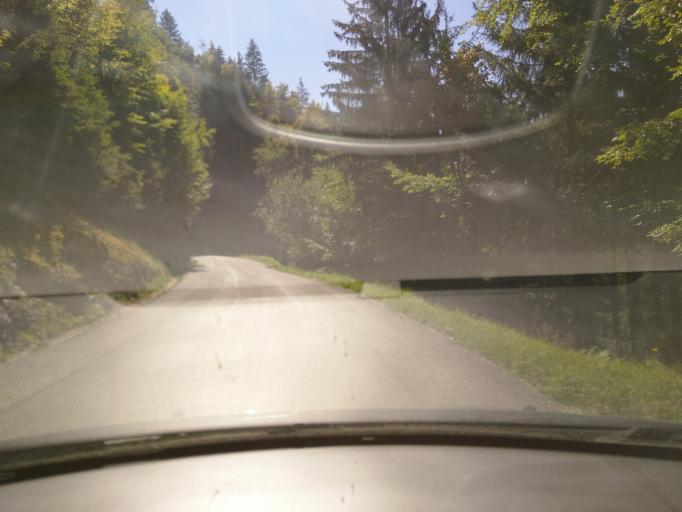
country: FR
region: Rhone-Alpes
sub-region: Departement de la Haute-Savoie
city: Praz-sur-Arly
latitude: 45.7958
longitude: 6.4982
